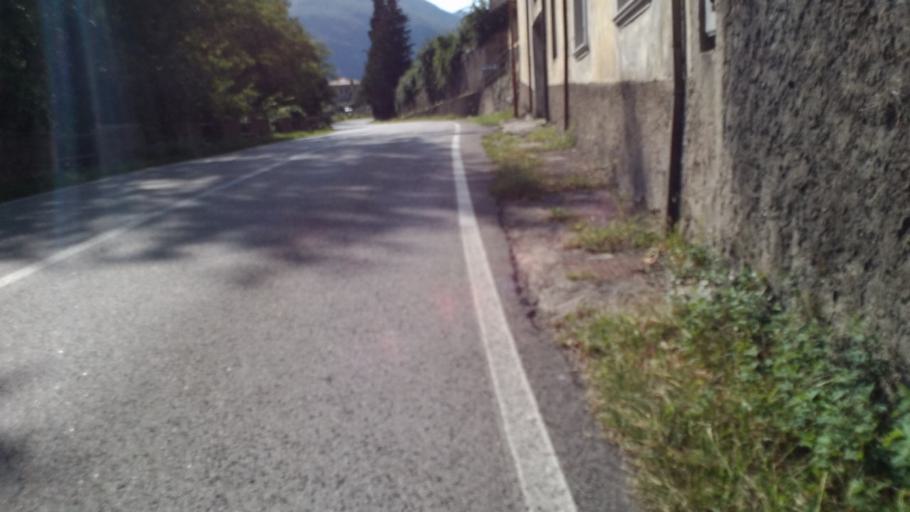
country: IT
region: Veneto
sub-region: Provincia di Verona
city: Brentino Belluno
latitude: 45.6562
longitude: 10.8940
